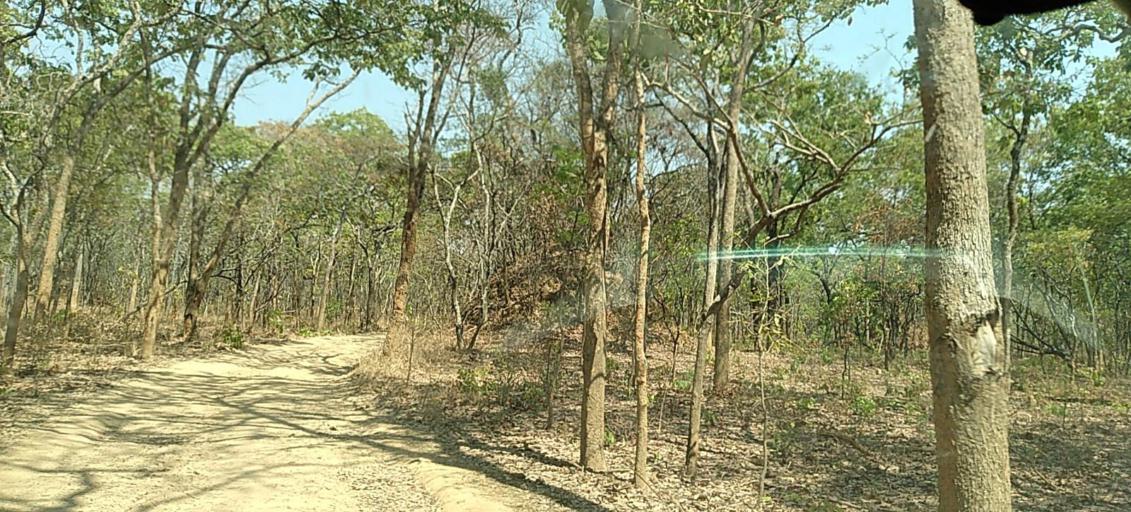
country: ZM
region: North-Western
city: Kasempa
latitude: -13.3918
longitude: 25.6283
